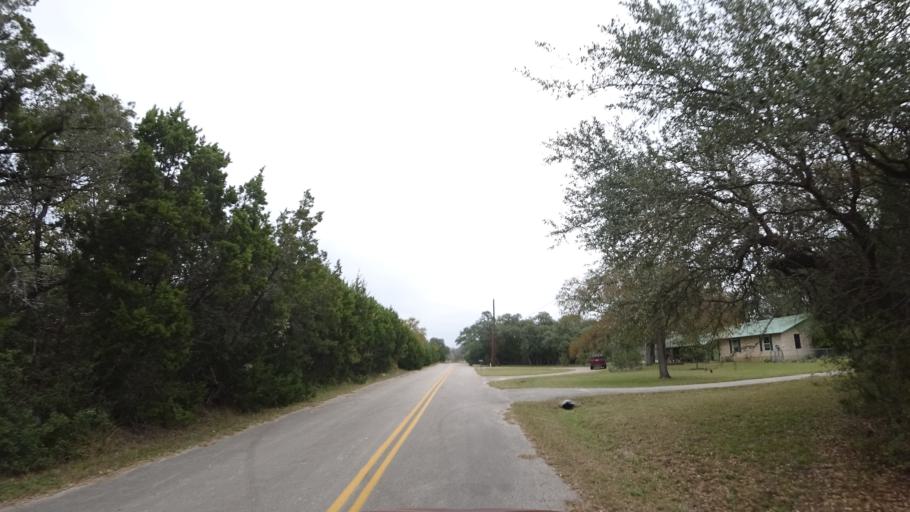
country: US
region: Texas
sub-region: Williamson County
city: Anderson Mill
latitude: 30.4519
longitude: -97.8338
